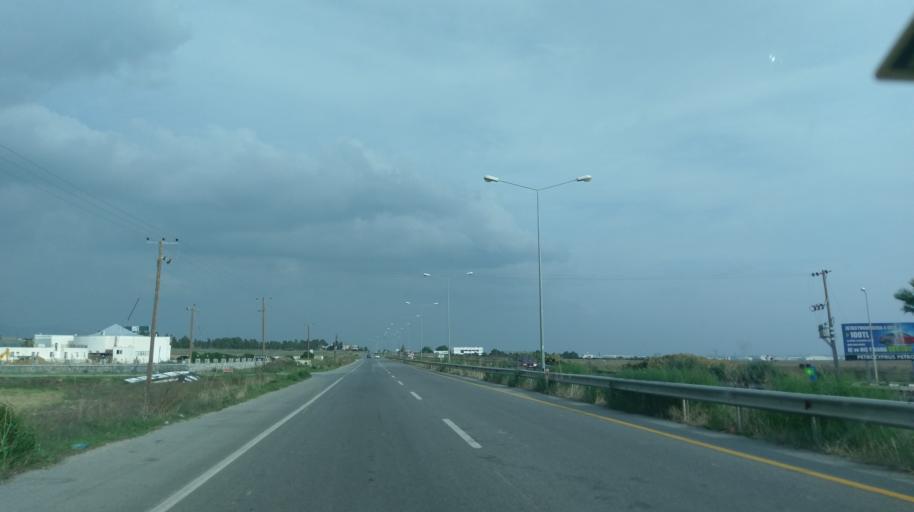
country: CY
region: Lefkosia
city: Mammari
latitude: 35.2119
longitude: 33.2446
